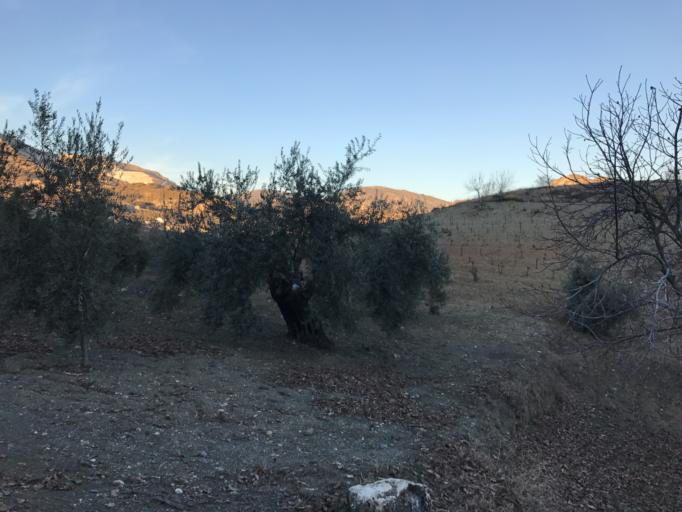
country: ES
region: Andalusia
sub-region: Provincia de Granada
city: Beas de Granada
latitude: 37.2179
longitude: -3.4868
